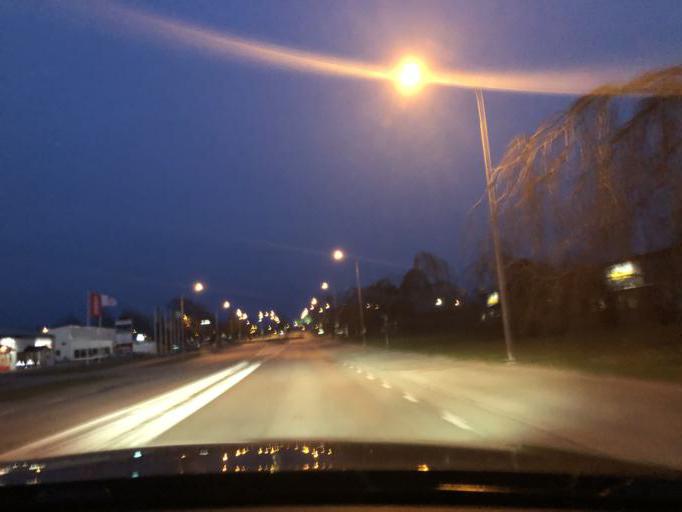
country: SE
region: Kalmar
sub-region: Kalmar Kommun
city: Kalmar
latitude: 56.6762
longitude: 16.3196
